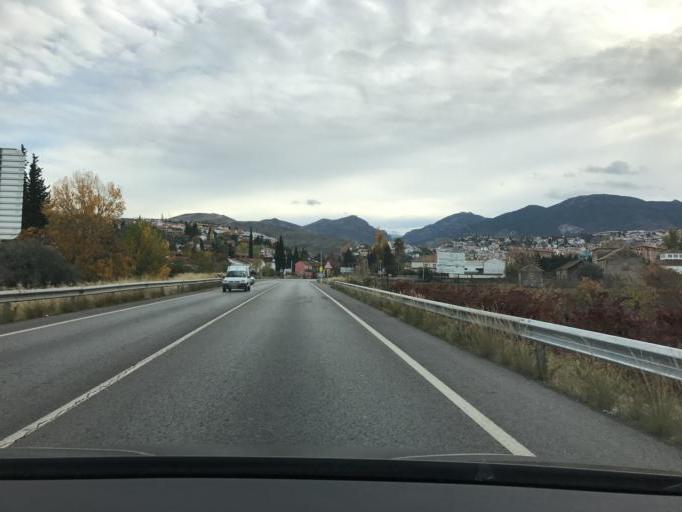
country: ES
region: Andalusia
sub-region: Provincia de Granada
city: Huetor Vega
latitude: 37.1405
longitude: -3.5725
